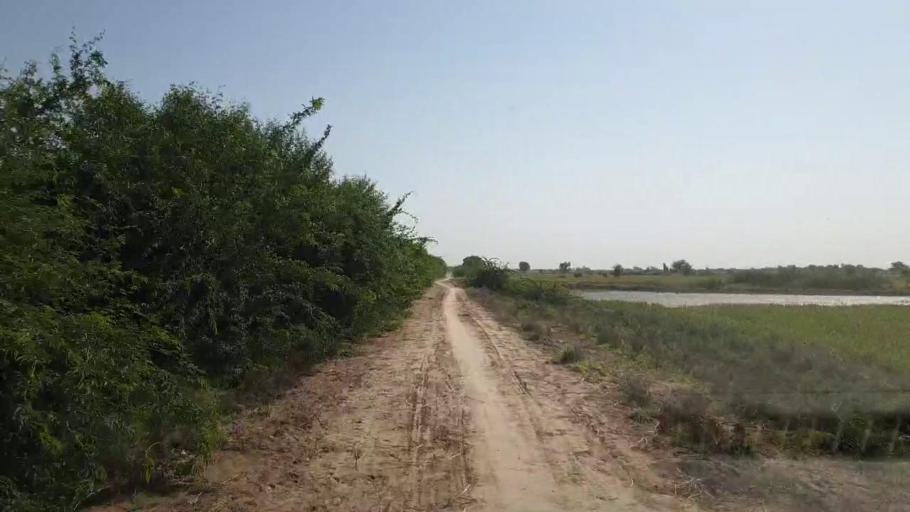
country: PK
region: Sindh
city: Kadhan
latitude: 24.6037
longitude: 69.0037
